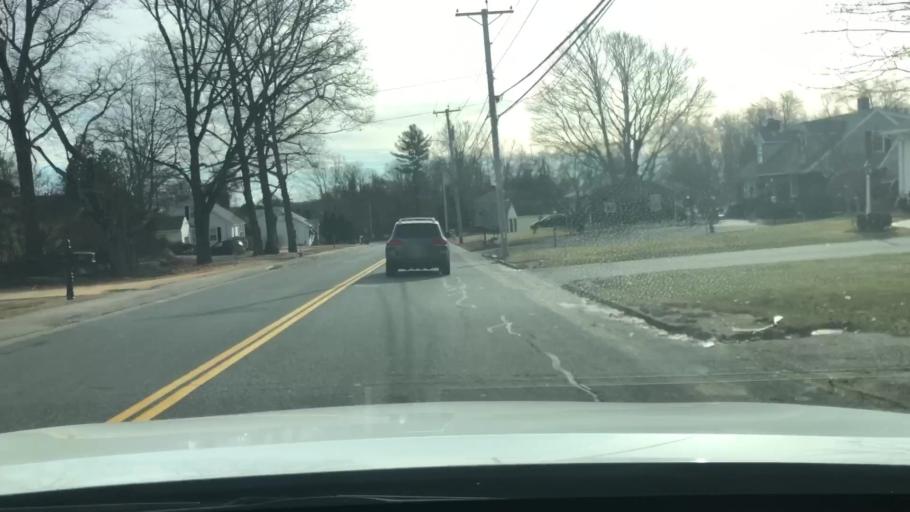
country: US
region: Massachusetts
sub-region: Worcester County
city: Hopedale
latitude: 42.1431
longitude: -71.5368
